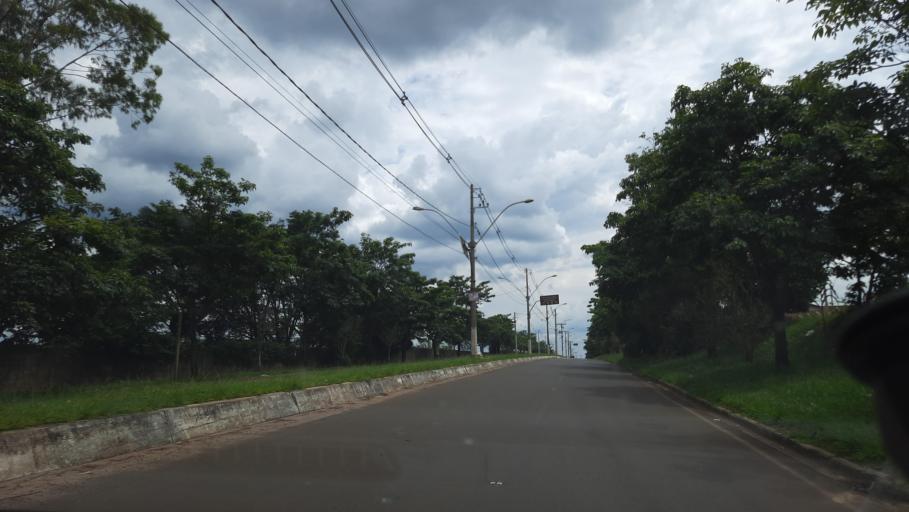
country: BR
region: Sao Paulo
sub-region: Cajuru
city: Cajuru
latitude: -21.2738
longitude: -47.2910
